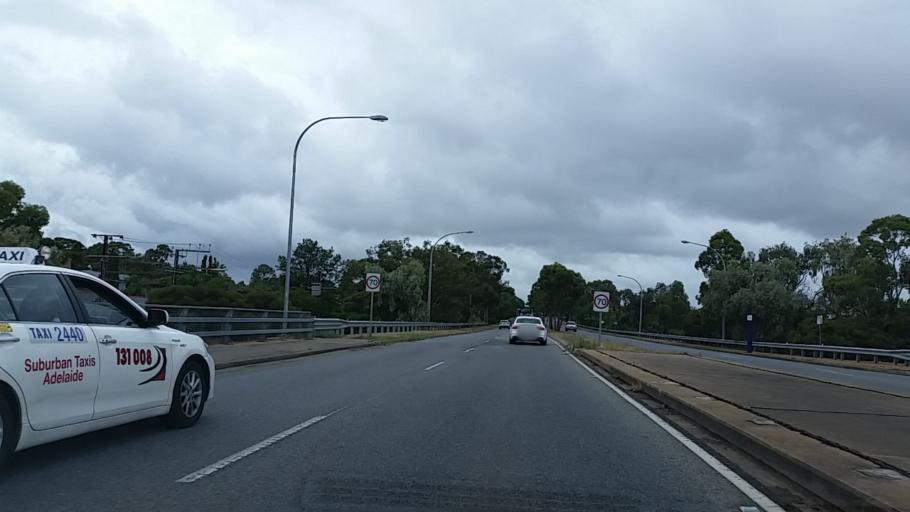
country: AU
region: South Australia
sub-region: Salisbury
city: Ingle Farm
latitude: -34.8307
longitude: 138.6460
